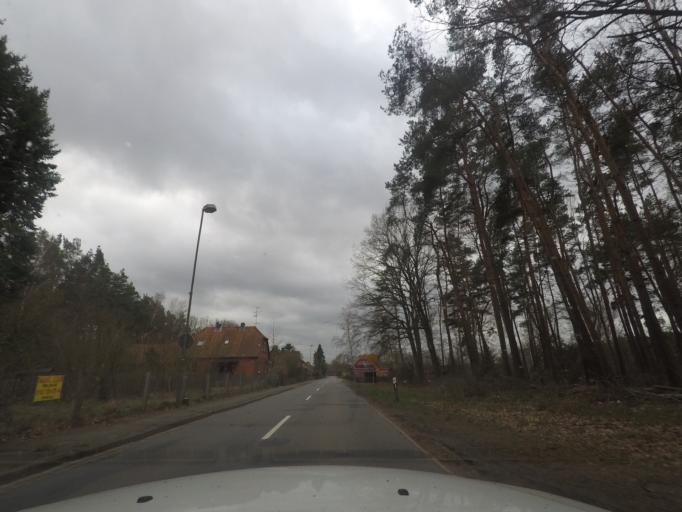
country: DE
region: Lower Saxony
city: Bad Bevensen
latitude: 53.0501
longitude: 10.6057
